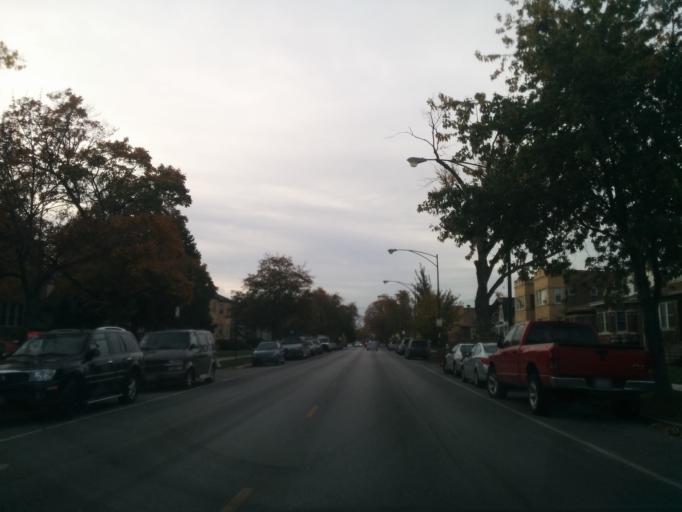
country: US
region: Illinois
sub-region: Cook County
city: Elmwood Park
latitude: 41.9126
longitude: -87.7851
